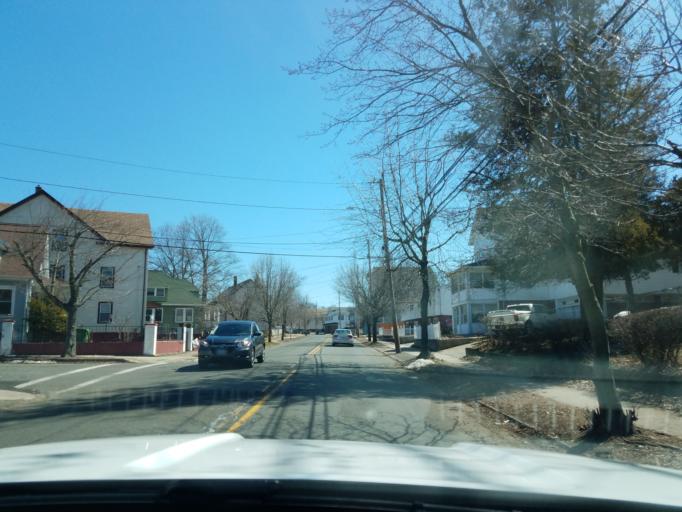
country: US
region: Connecticut
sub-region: New Haven County
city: Wallingford
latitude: 41.4546
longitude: -72.8312
